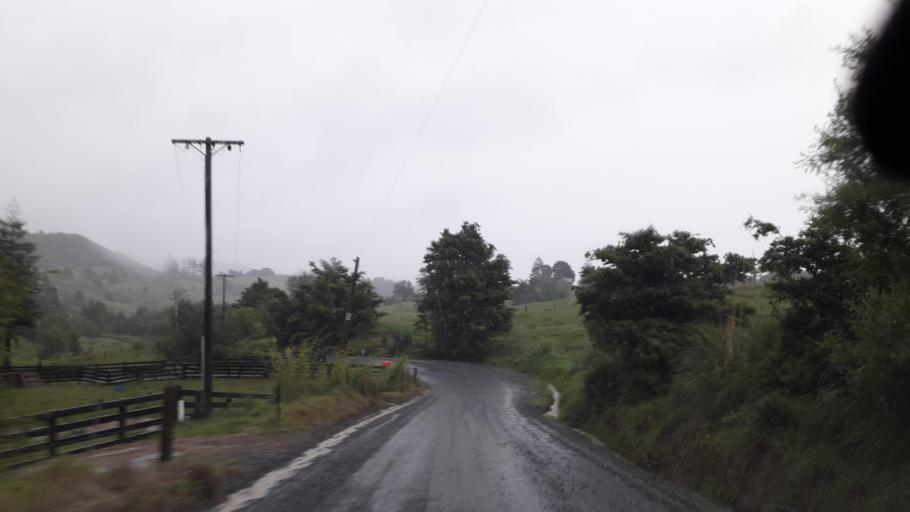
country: NZ
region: Northland
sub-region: Far North District
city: Kerikeri
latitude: -35.1287
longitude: 173.7426
